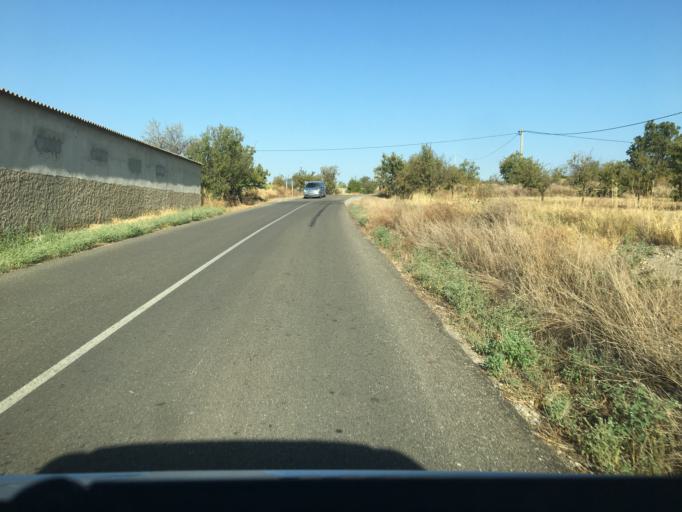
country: ES
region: Andalusia
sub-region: Provincia de Almeria
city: Huercal-Overa
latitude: 37.4702
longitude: -1.9006
